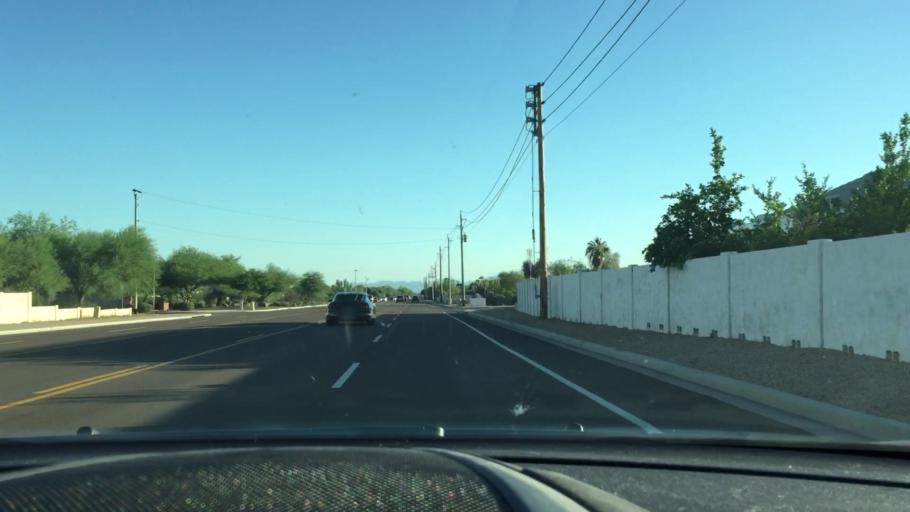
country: US
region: Arizona
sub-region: Maricopa County
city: Sun City
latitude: 33.6933
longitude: -112.2377
